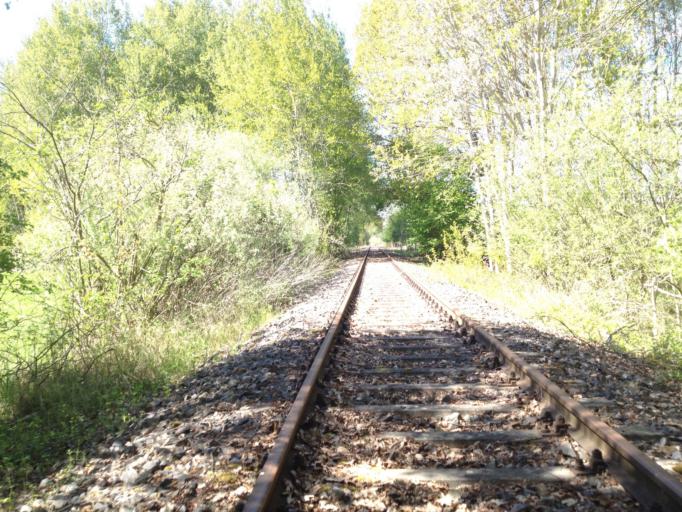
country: DE
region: Brandenburg
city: Templin
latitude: 53.1287
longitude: 13.4417
